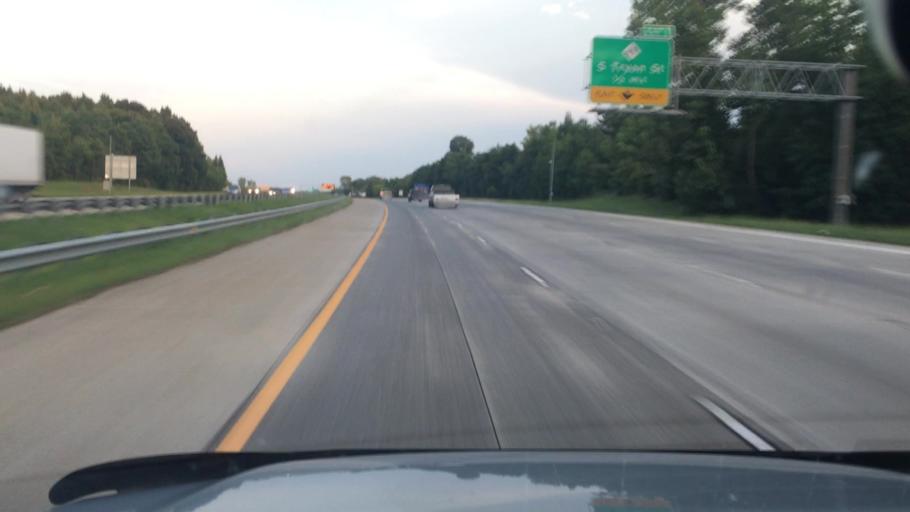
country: US
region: North Carolina
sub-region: Mecklenburg County
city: Pineville
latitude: 35.1495
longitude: -80.9438
